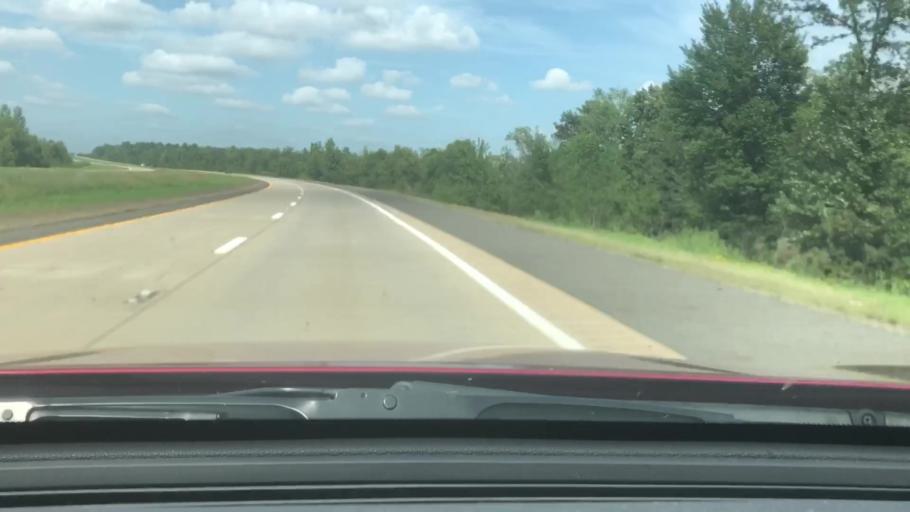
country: US
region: Texas
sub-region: Cass County
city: Queen City
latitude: 33.1681
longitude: -93.8795
